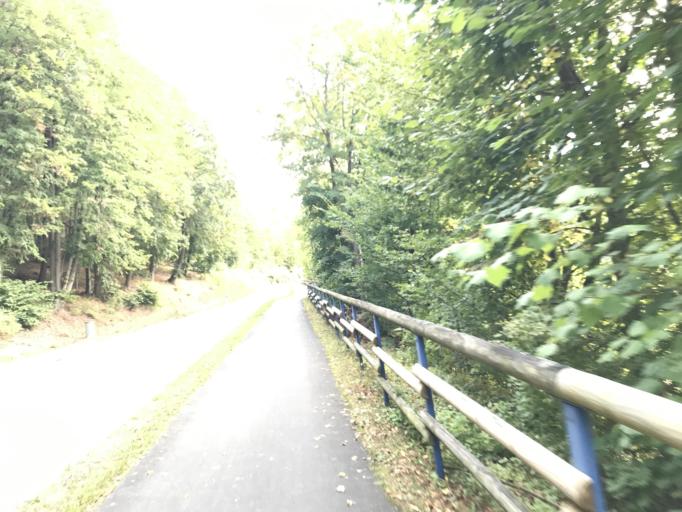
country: DE
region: Hesse
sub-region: Regierungsbezirk Kassel
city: Sachsenhausen
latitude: 51.1959
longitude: 9.0064
